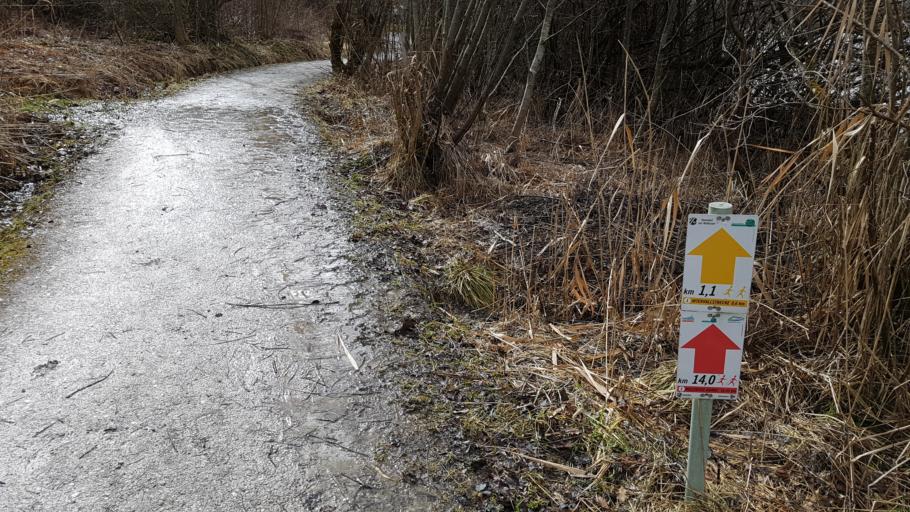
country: AT
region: Salzburg
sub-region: Politischer Bezirk Salzburg-Umgebung
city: Henndorf am Wallersee
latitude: 47.9035
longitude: 13.1728
